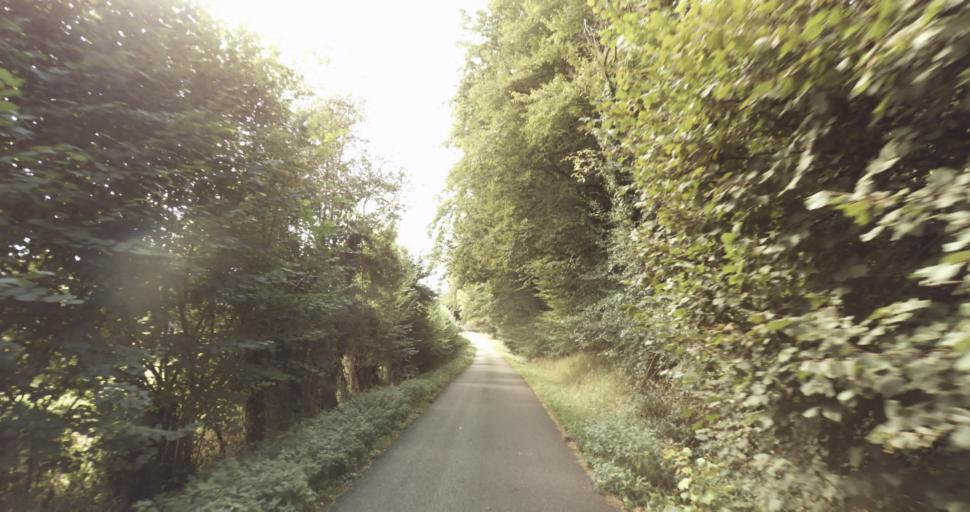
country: FR
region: Lower Normandy
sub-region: Departement de l'Orne
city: Gace
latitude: 48.7992
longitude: 0.2657
